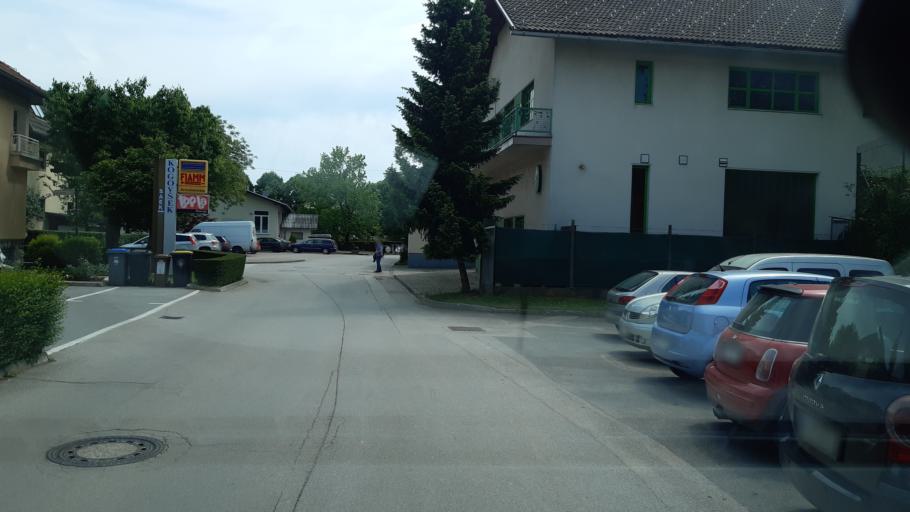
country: SI
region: Ljubljana
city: Ljubljana
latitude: 46.0839
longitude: 14.4724
